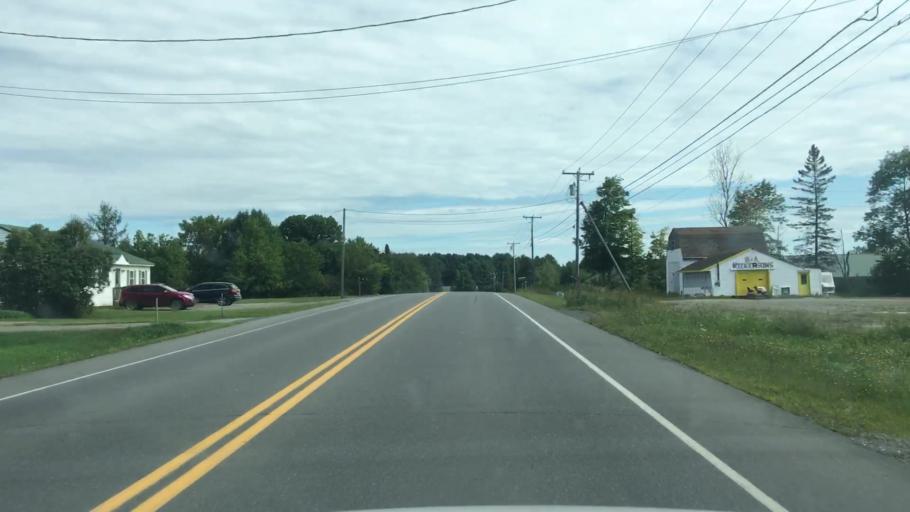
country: US
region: Maine
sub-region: Piscataquis County
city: Dover-Foxcroft
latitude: 45.1962
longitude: -69.2119
